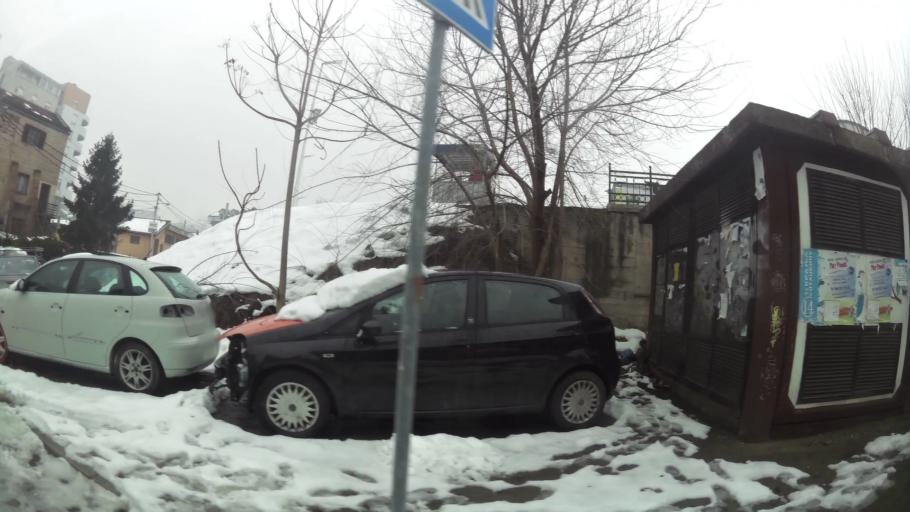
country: RS
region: Central Serbia
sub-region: Belgrade
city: Zvezdara
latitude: 44.7824
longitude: 20.5215
